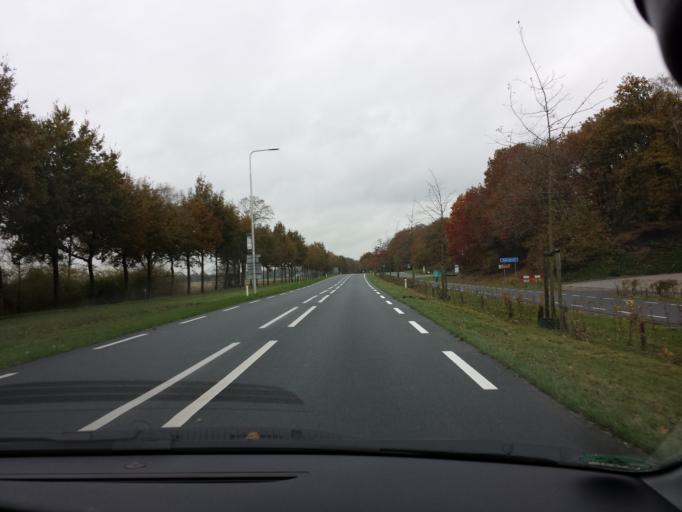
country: NL
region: Limburg
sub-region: Gemeente Venlo
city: Arcen
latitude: 51.4957
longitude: 6.1778
